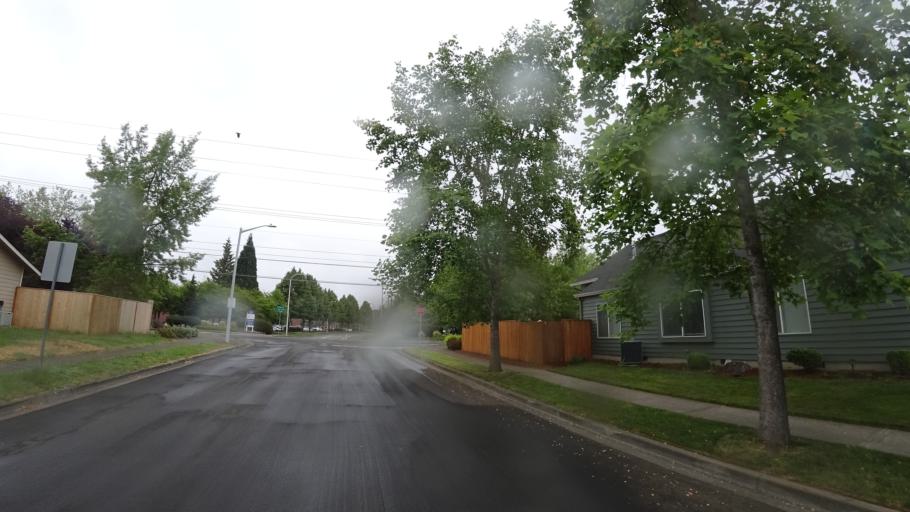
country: US
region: Oregon
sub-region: Washington County
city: Rockcreek
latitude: 45.5314
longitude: -122.8895
